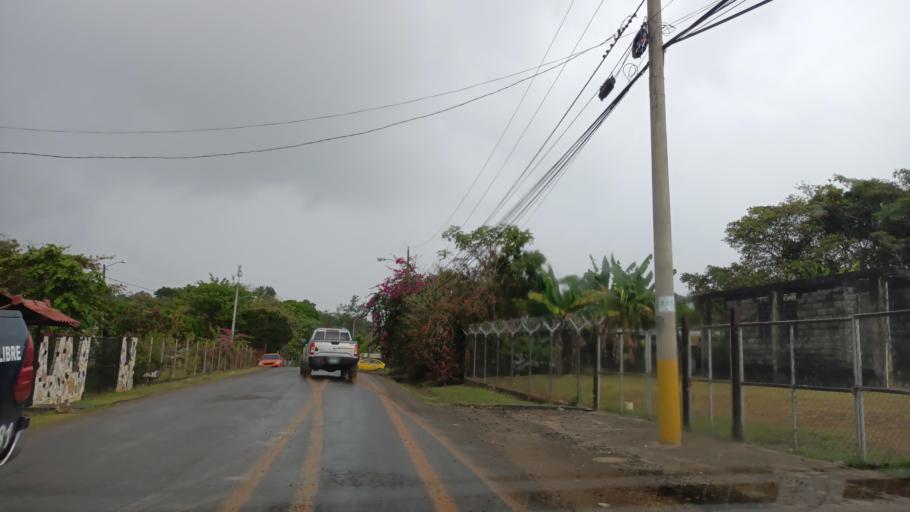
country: PA
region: Panama
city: Caimitillo
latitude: 9.1646
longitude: -79.5496
